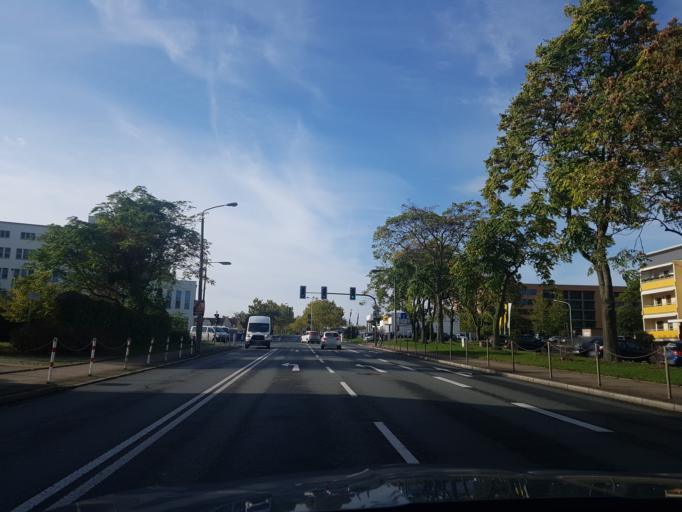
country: DE
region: Saxony
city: Riesa
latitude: 51.3067
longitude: 13.2920
